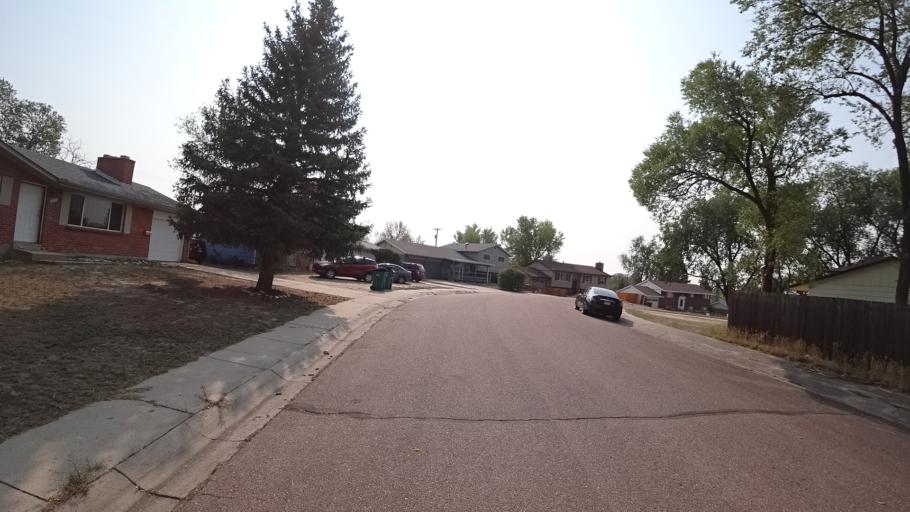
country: US
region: Colorado
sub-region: El Paso County
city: Stratmoor
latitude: 38.8150
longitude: -104.7729
